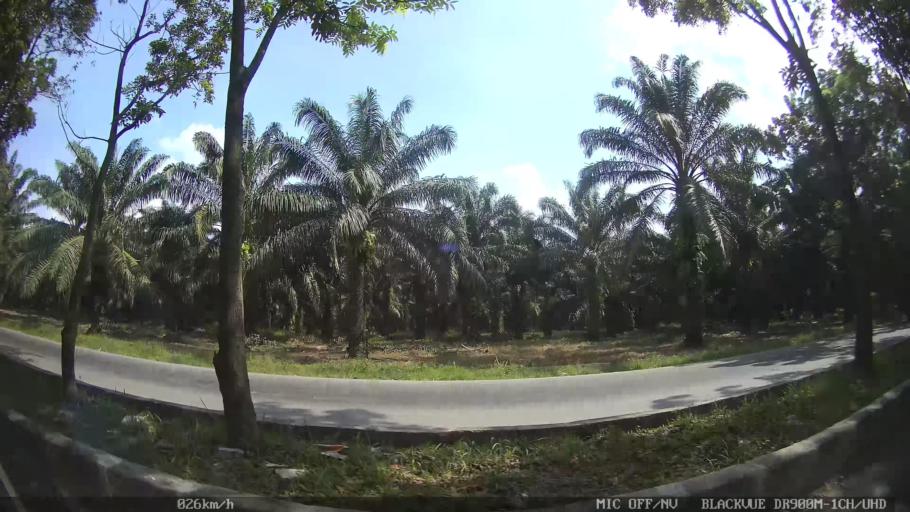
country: ID
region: North Sumatra
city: Binjai
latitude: 3.6507
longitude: 98.5195
